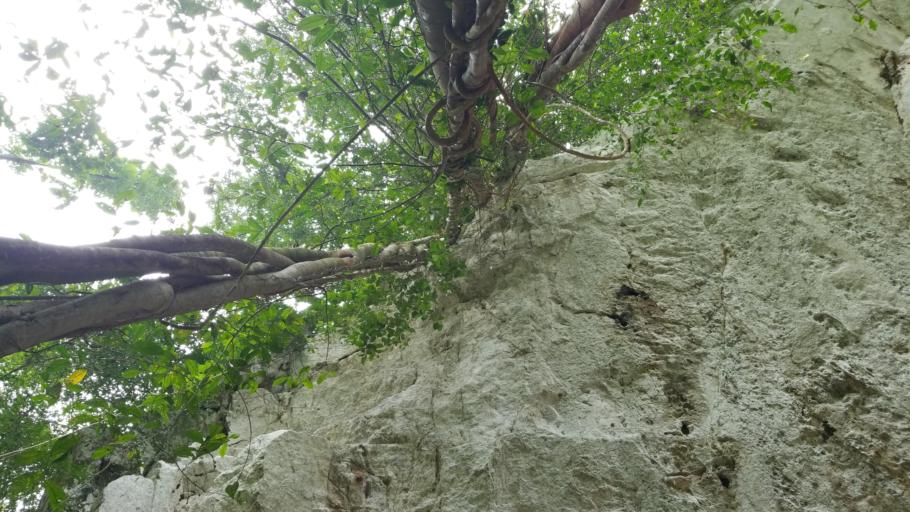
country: TH
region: Yala
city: Betong
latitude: 5.6696
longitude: 100.8739
